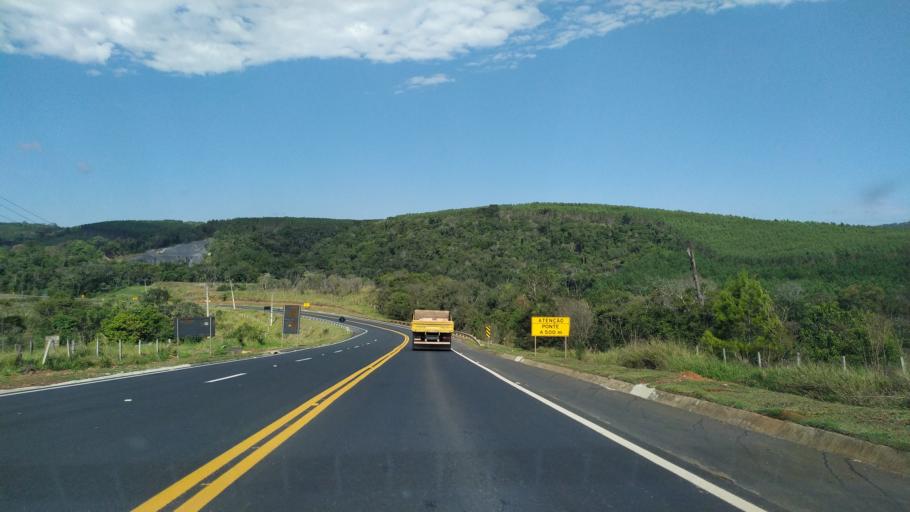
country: BR
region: Parana
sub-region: Telemaco Borba
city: Telemaco Borba
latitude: -24.2878
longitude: -50.7051
